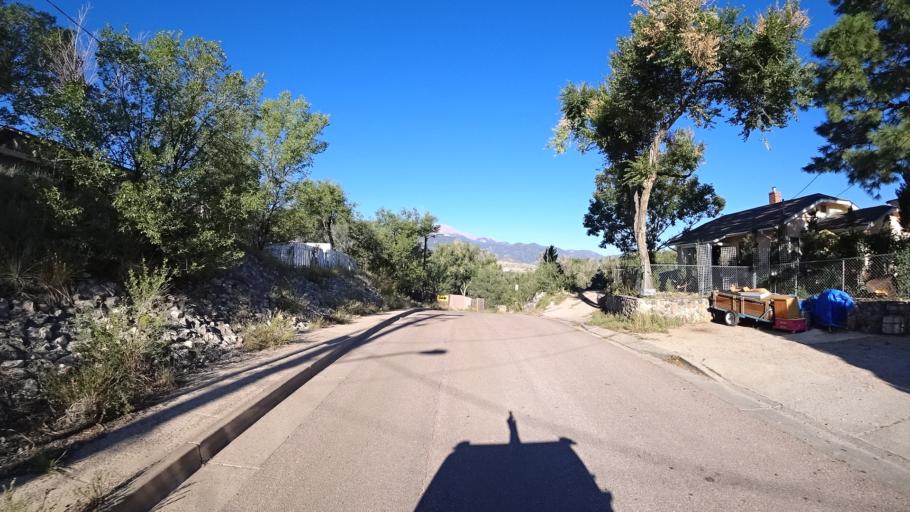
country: US
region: Colorado
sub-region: El Paso County
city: Colorado Springs
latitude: 38.8376
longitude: -104.8388
